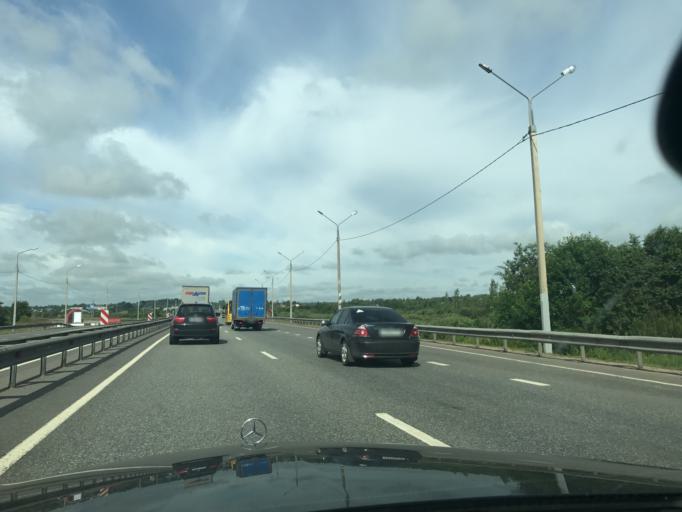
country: RU
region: Smolensk
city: Yartsevo
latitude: 55.0791
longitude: 32.6966
